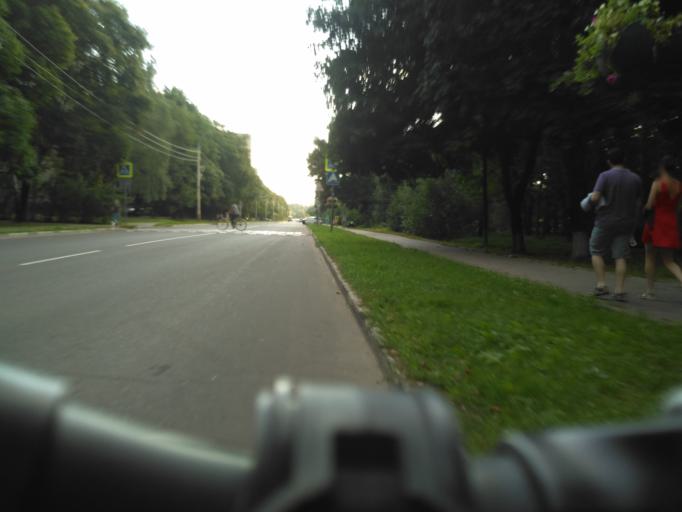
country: RU
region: Moskovskaya
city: Dubna
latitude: 56.7466
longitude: 37.1805
